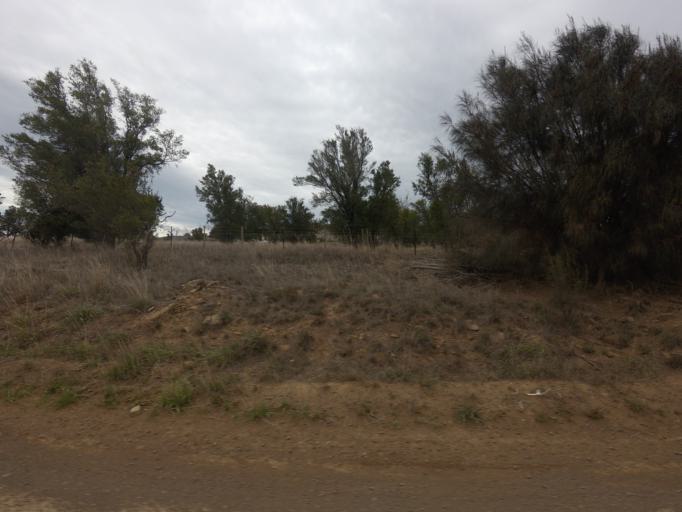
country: AU
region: Tasmania
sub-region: Derwent Valley
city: New Norfolk
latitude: -42.5545
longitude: 146.9102
